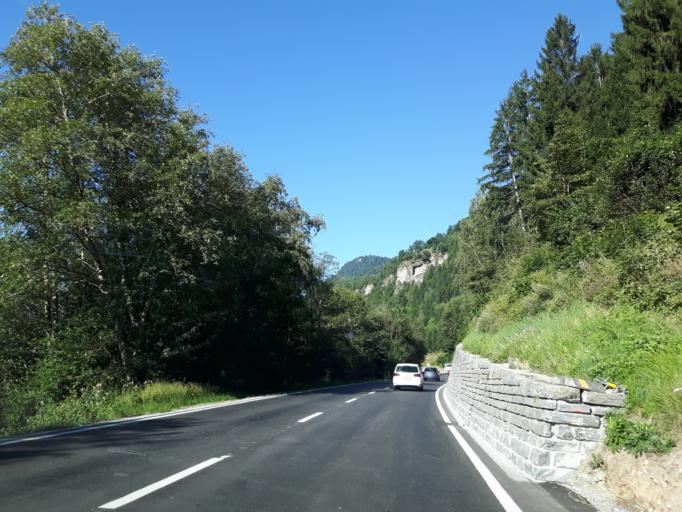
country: CH
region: Grisons
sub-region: Surselva District
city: Breil
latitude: 46.7749
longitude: 9.1321
